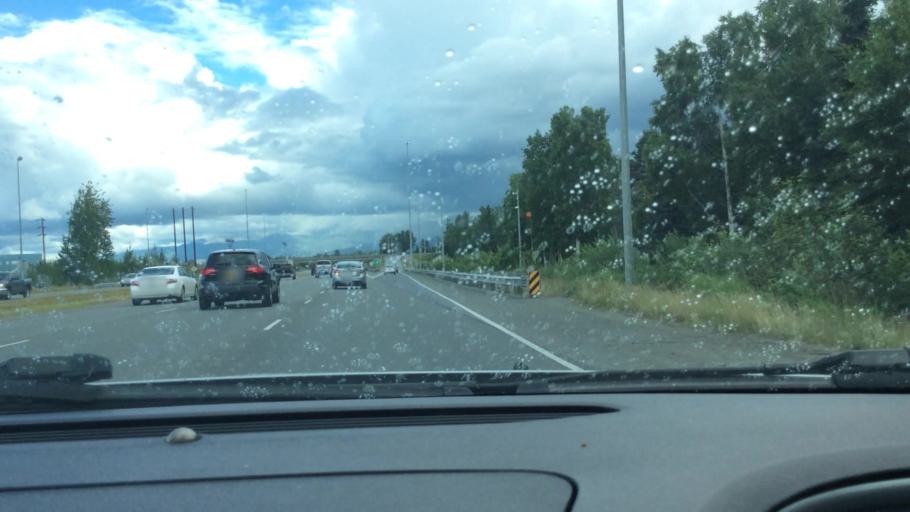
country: US
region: Alaska
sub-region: Anchorage Municipality
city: Anchorage
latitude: 61.2188
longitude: -149.8165
